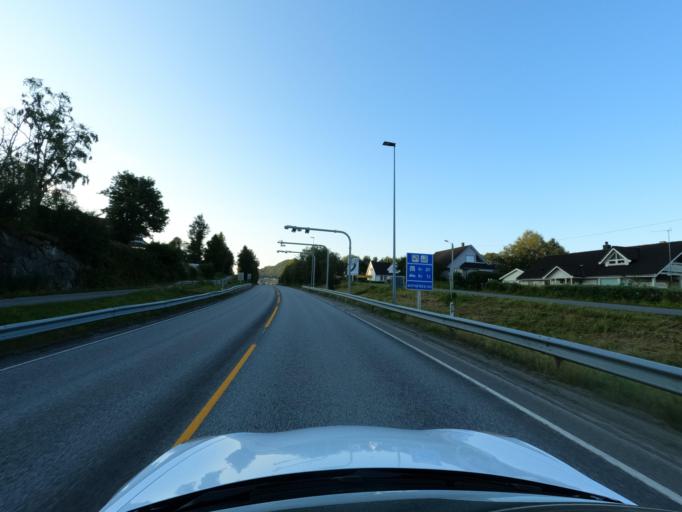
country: NO
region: Troms
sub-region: Harstad
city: Harstad
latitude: 68.7760
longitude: 16.5634
